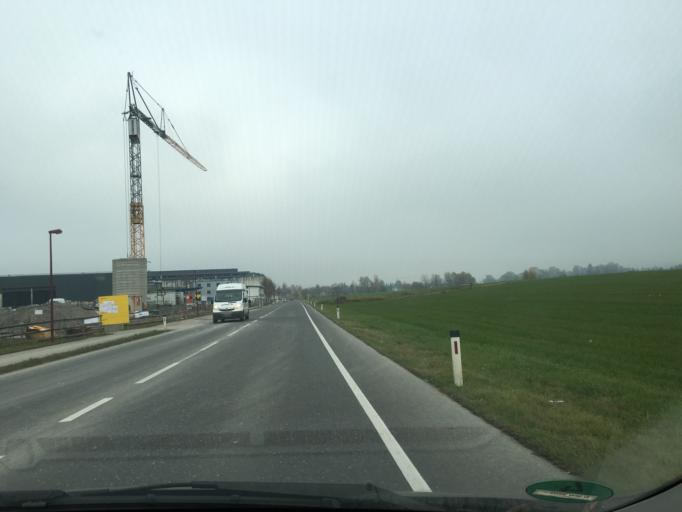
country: AT
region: Vorarlberg
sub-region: Politischer Bezirk Feldkirch
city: Altach
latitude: 47.3463
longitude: 9.6571
